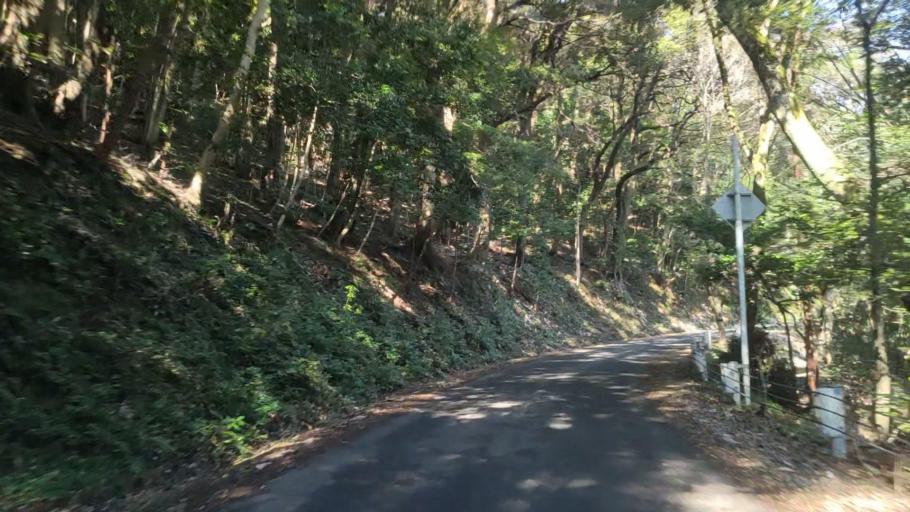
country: JP
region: Gifu
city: Gifu-shi
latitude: 35.4287
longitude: 136.7722
